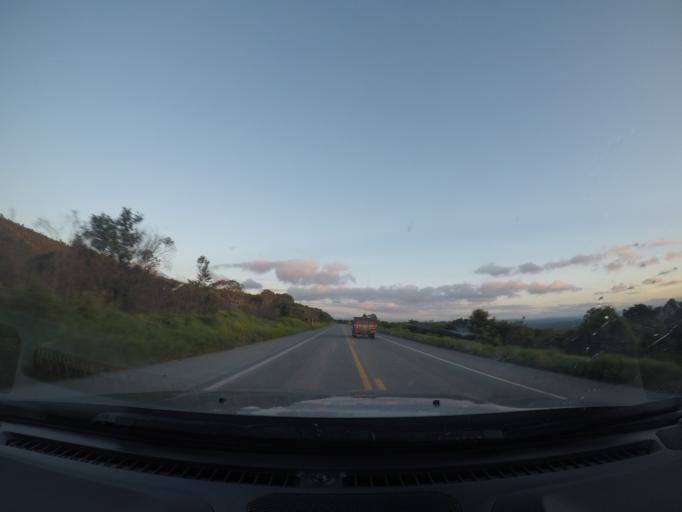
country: BR
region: Bahia
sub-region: Seabra
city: Seabra
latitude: -12.4293
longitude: -41.8282
